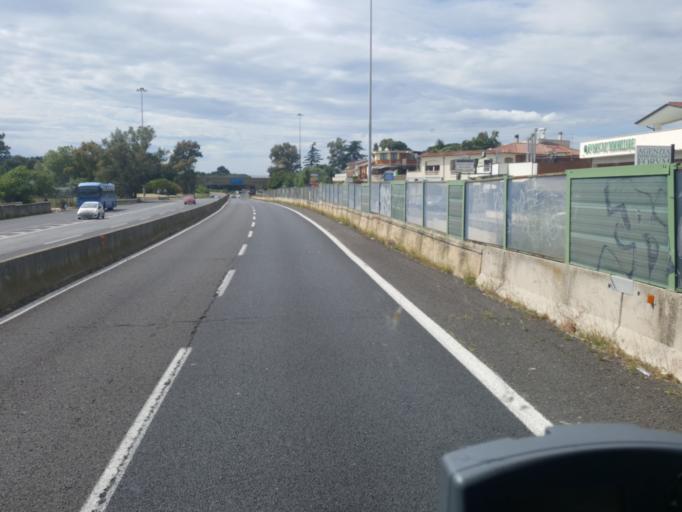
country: IT
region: Latium
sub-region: Citta metropolitana di Roma Capitale
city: Ara Nova
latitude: 41.9171
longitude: 12.2404
